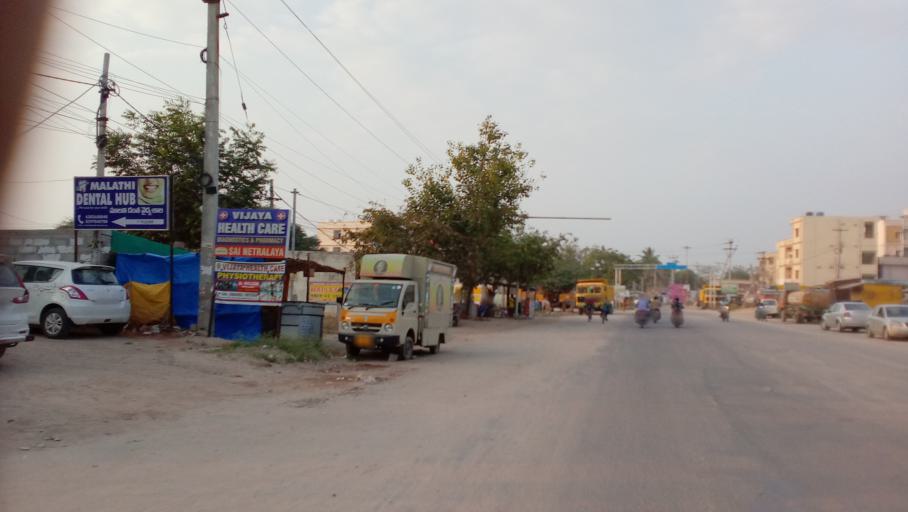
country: IN
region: Telangana
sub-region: Medak
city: Serilingampalle
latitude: 17.5077
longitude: 78.3184
